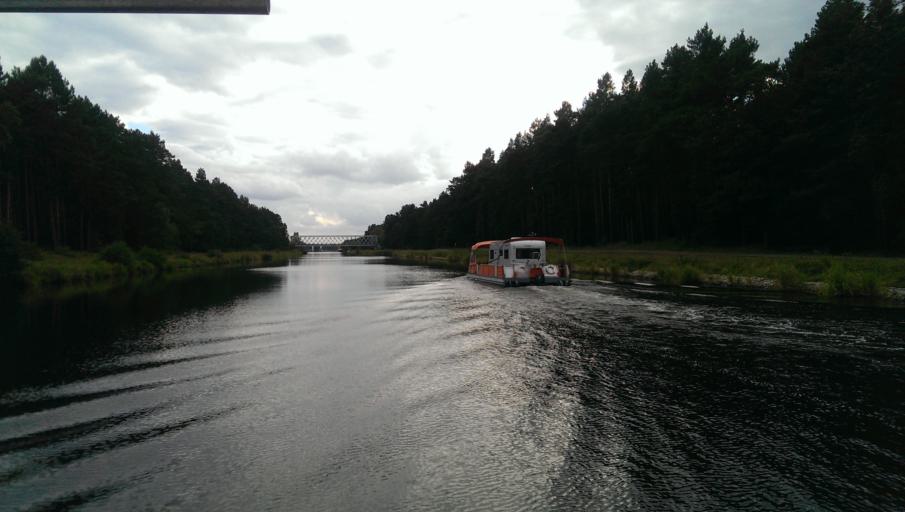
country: DE
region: Brandenburg
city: Oranienburg
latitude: 52.7828
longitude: 13.2804
